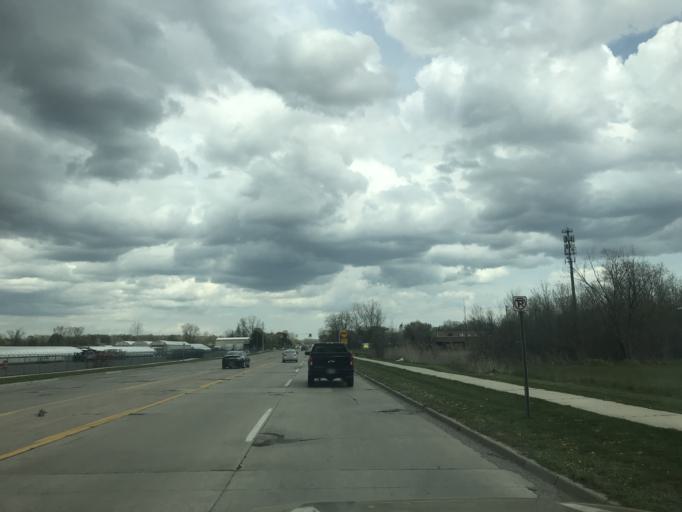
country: US
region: Michigan
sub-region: Wayne County
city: Taylor
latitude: 42.1955
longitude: -83.3234
